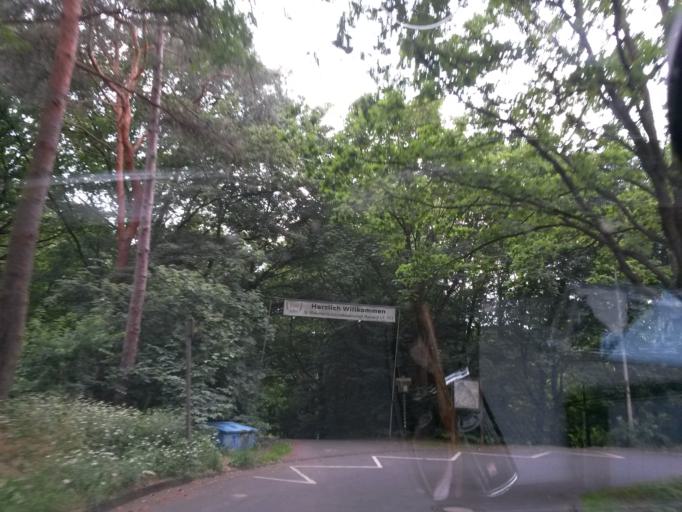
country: DE
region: North Rhine-Westphalia
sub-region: Regierungsbezirk Koln
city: Alfter
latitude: 50.7047
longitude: 7.0410
